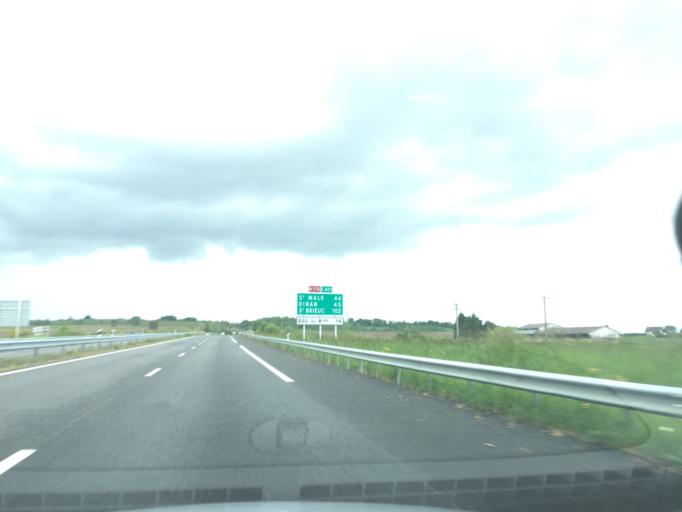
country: FR
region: Brittany
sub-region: Departement d'Ille-et-Vilaine
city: Pleine-Fougeres
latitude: 48.5631
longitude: -1.5509
